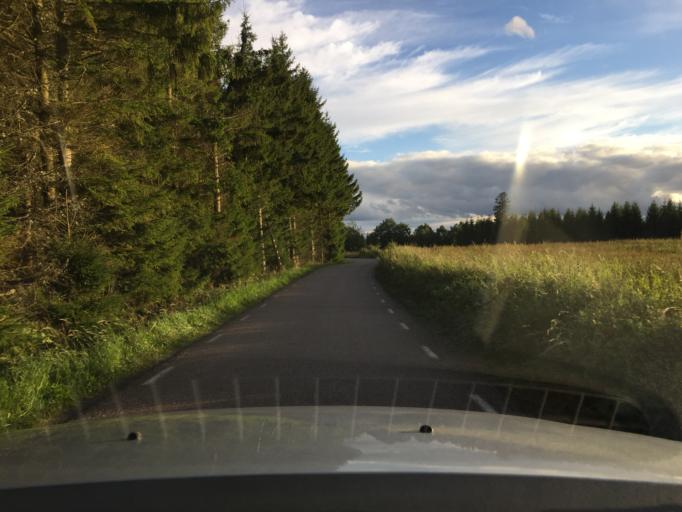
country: SE
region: Skane
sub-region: Hassleholms Kommun
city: Tormestorp
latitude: 56.0196
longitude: 13.7754
